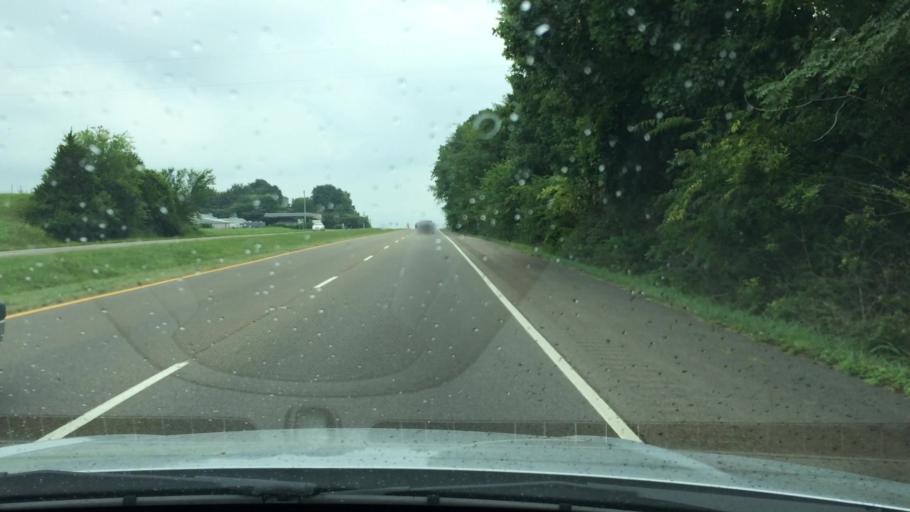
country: US
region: Tennessee
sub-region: Jefferson County
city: New Market
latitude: 36.1079
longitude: -83.5230
